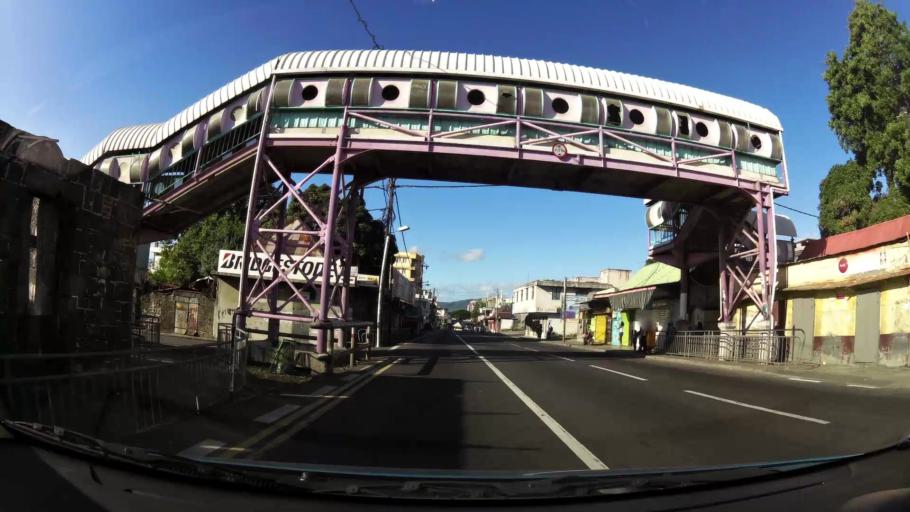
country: MU
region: Port Louis
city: Port Louis
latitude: -20.1664
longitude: 57.4892
